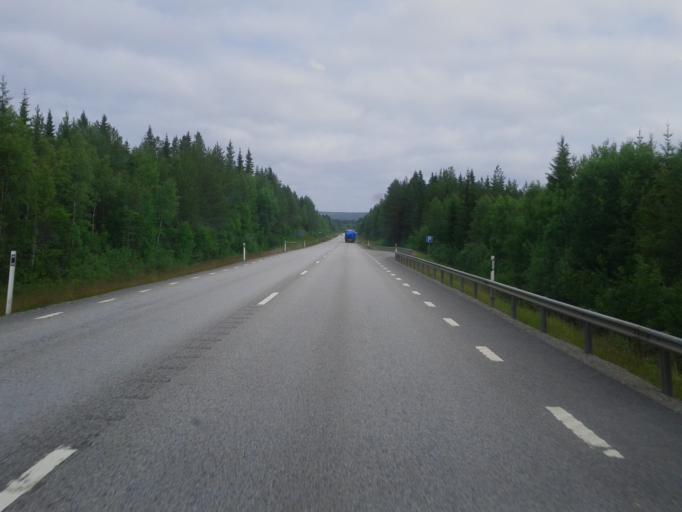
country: SE
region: Vaesterbotten
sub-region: Robertsfors Kommun
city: Robertsfors
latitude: 64.2831
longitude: 21.0681
